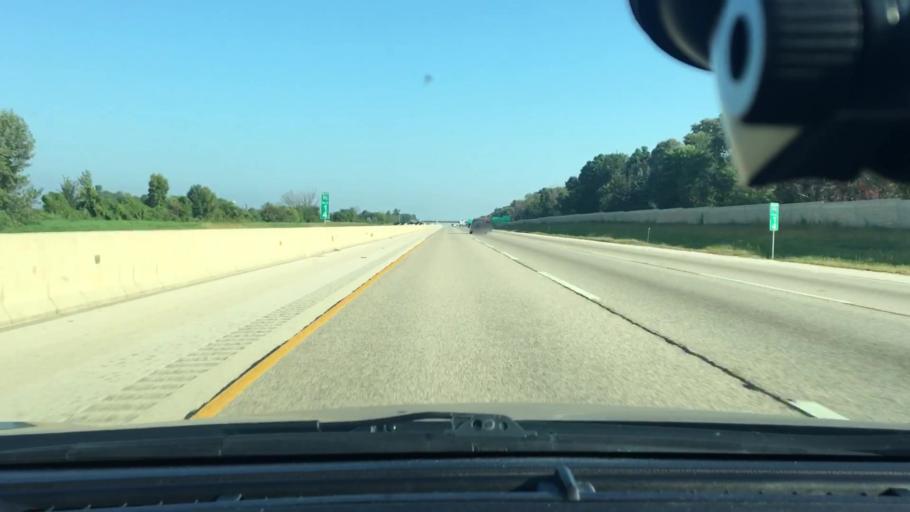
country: US
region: Illinois
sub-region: Winnebago County
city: Cherry Valley
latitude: 42.2965
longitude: -88.9647
